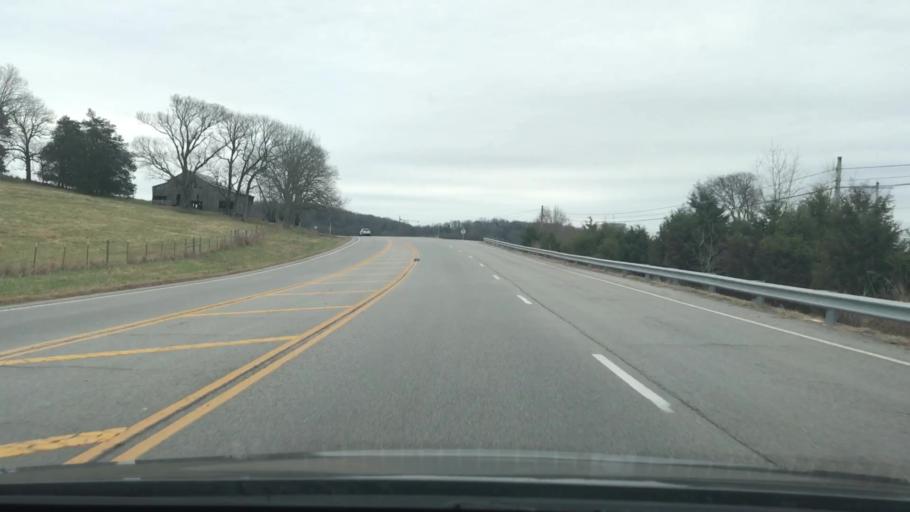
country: US
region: Tennessee
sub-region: Trousdale County
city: Hartsville
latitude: 36.3730
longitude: -86.1078
